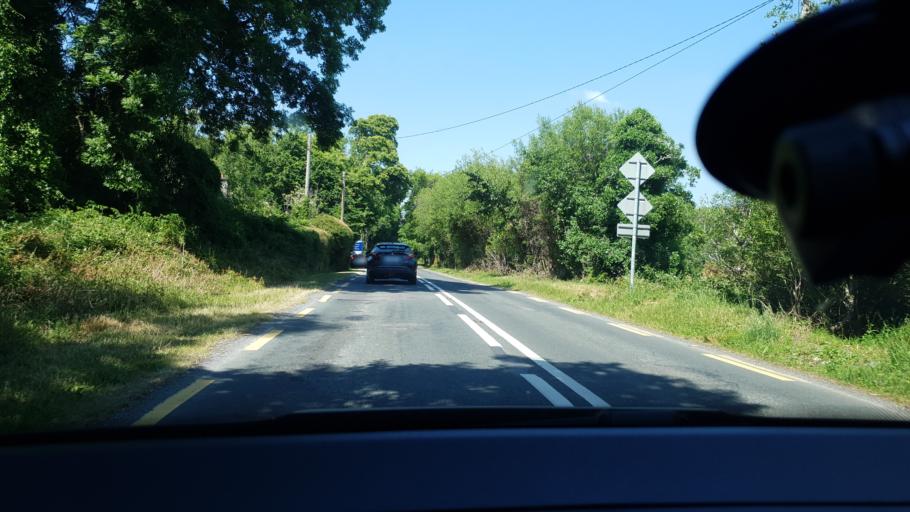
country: IE
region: Munster
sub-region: Ciarrai
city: Cill Airne
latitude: 52.0164
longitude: -9.4942
